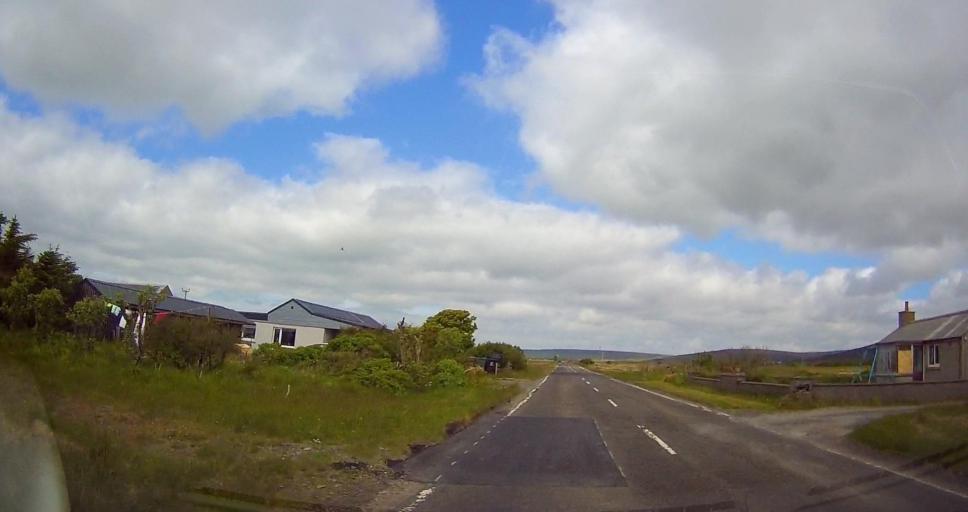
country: GB
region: Scotland
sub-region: Orkney Islands
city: Stromness
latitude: 59.0182
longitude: -3.1569
